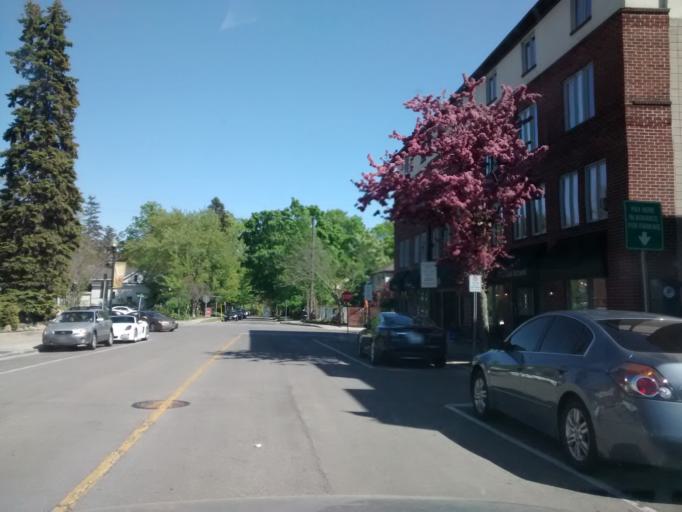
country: CA
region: Ontario
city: Oakville
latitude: 43.4463
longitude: -79.6671
